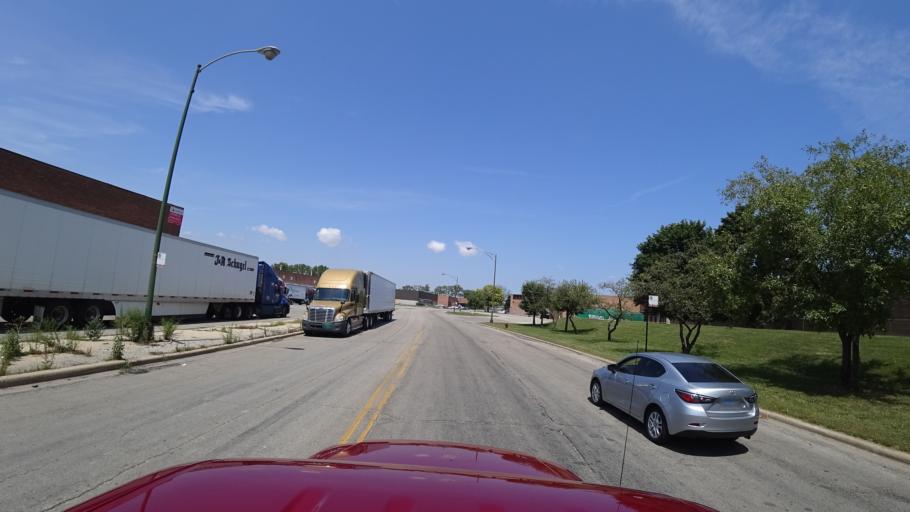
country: US
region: Illinois
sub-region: Cook County
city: Chicago
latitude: 41.8188
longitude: -87.6555
